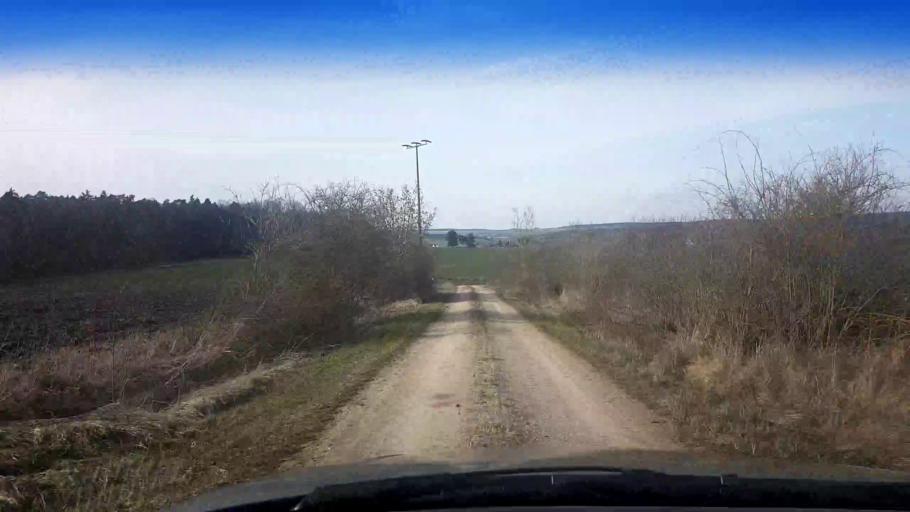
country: DE
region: Bavaria
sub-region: Upper Franconia
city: Burgebrach
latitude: 49.8105
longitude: 10.7479
